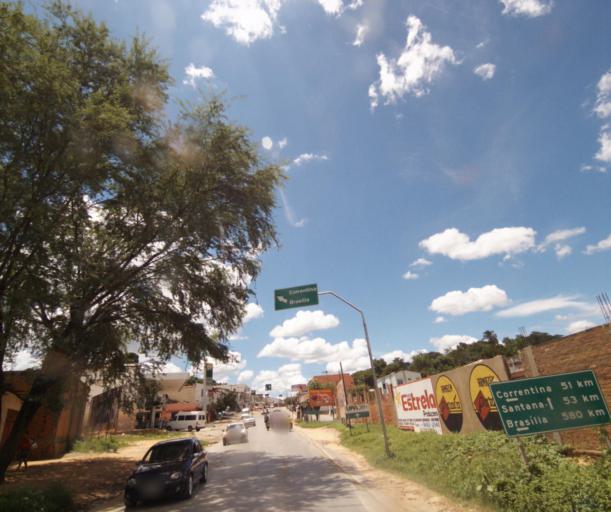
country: BR
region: Bahia
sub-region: Sao Felix Do Coribe
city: Santa Maria da Vitoria
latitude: -13.3991
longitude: -44.2024
